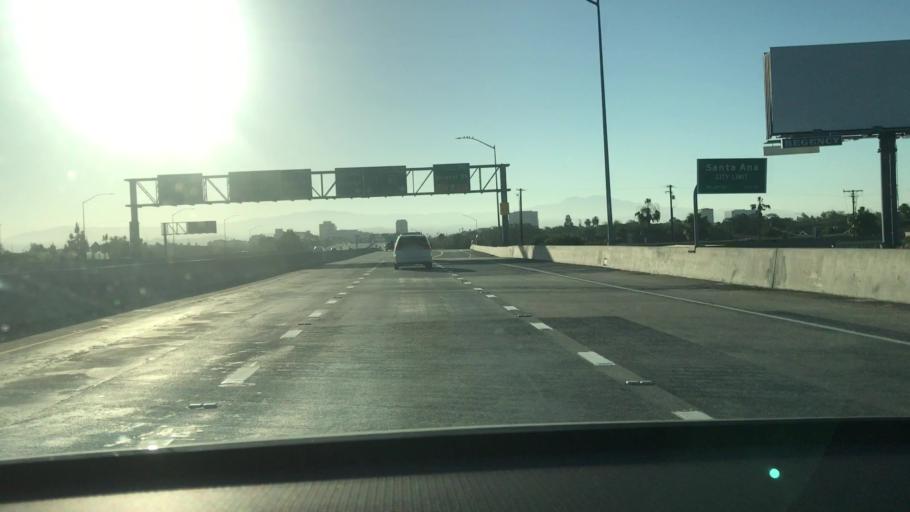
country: US
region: California
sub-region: Orange County
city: Orange
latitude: 33.7788
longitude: -117.8862
